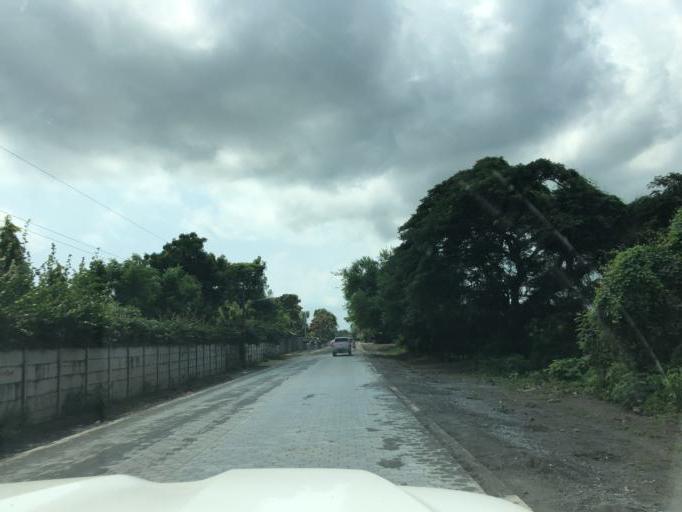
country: NI
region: Masaya
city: Tisma
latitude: 12.0367
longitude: -85.9228
